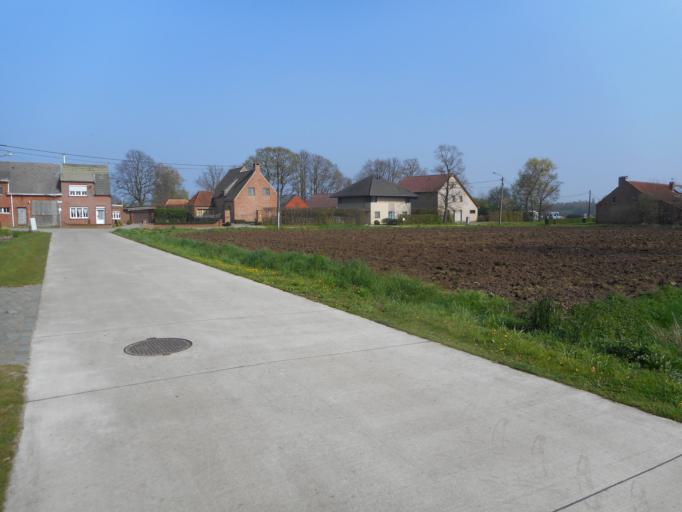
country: BE
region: Flanders
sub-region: Provincie Antwerpen
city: Kasterlee
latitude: 51.2194
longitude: 4.9362
